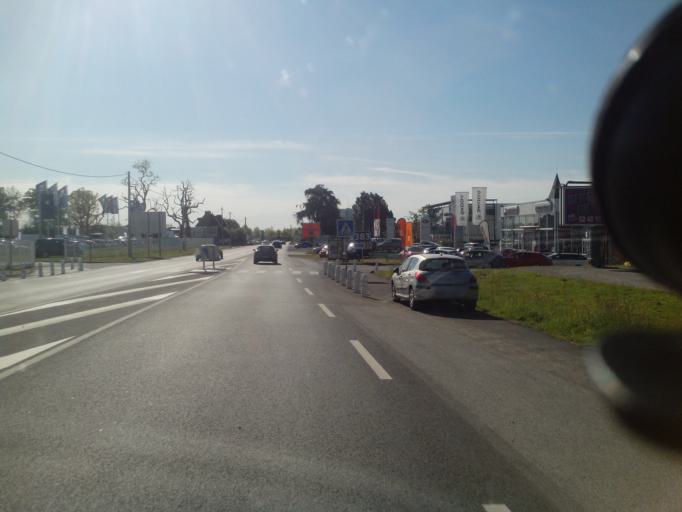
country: FR
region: Pays de la Loire
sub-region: Departement de la Loire-Atlantique
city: Orvault
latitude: 47.2538
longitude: -1.6271
